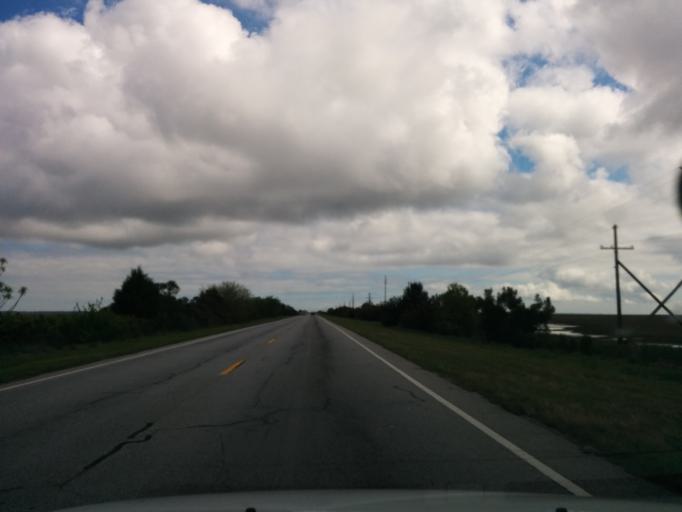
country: US
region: Georgia
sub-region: Glynn County
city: Brunswick
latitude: 31.0953
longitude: -81.4851
